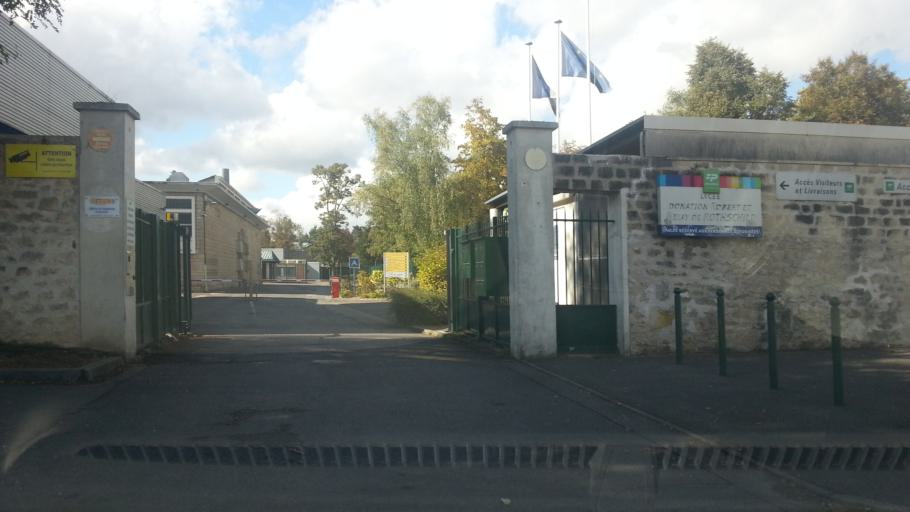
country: FR
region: Picardie
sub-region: Departement de l'Oise
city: Saint-Maximin
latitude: 49.2337
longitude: 2.4592
